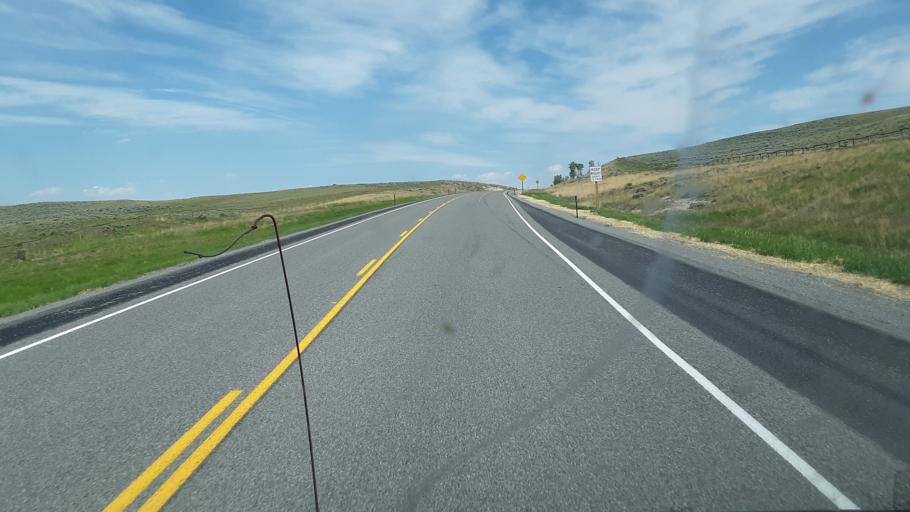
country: US
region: Wyoming
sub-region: Park County
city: Cody
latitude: 44.2581
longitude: -108.8674
